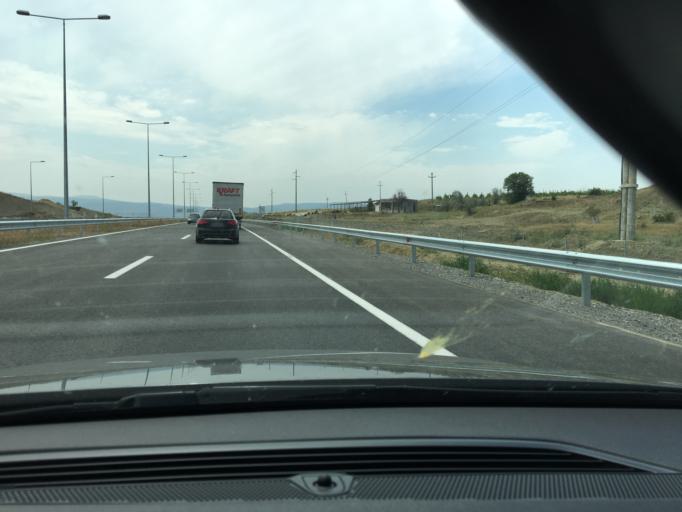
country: MK
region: Stip
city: Shtip
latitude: 41.7804
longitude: 22.1272
